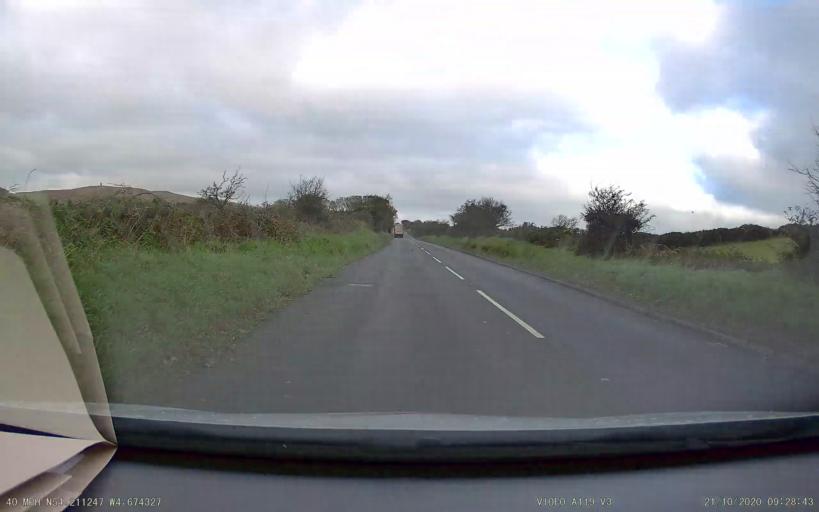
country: IM
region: Castletown
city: Castletown
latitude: 54.2112
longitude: -4.6743
